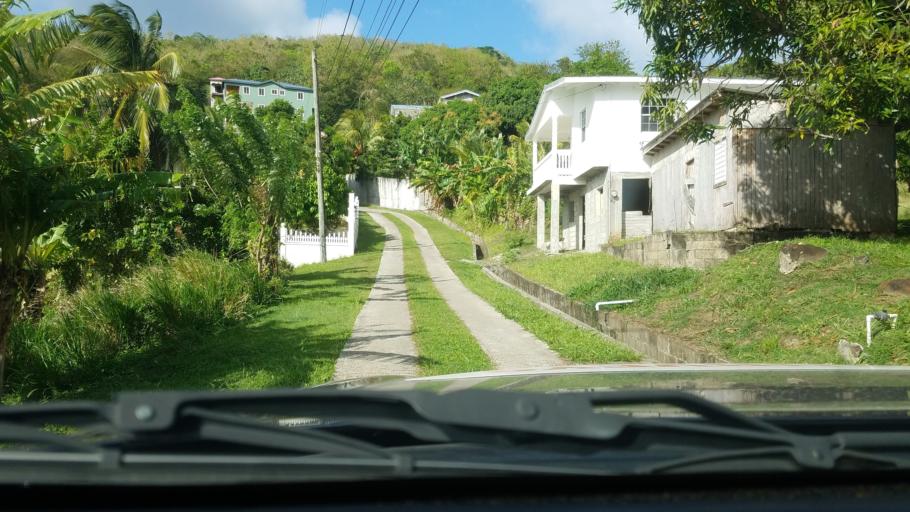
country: LC
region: Gros-Islet
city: Gros Islet
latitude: 14.0388
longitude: -60.9481
